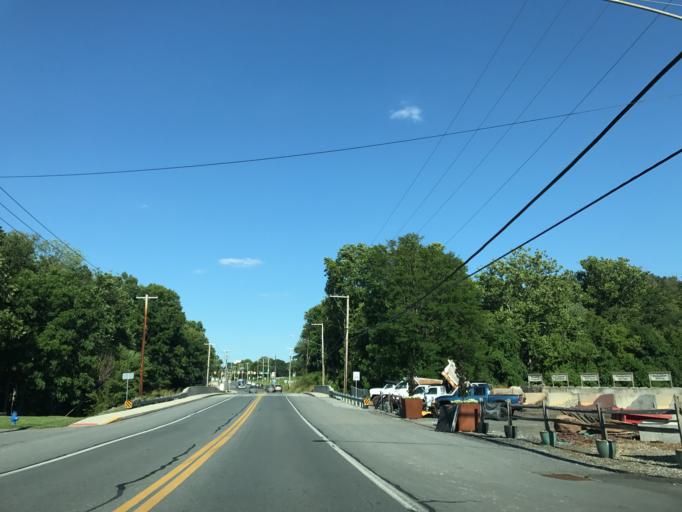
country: US
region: Pennsylvania
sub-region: Lancaster County
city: Mount Joy
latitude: 40.1090
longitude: -76.4912
